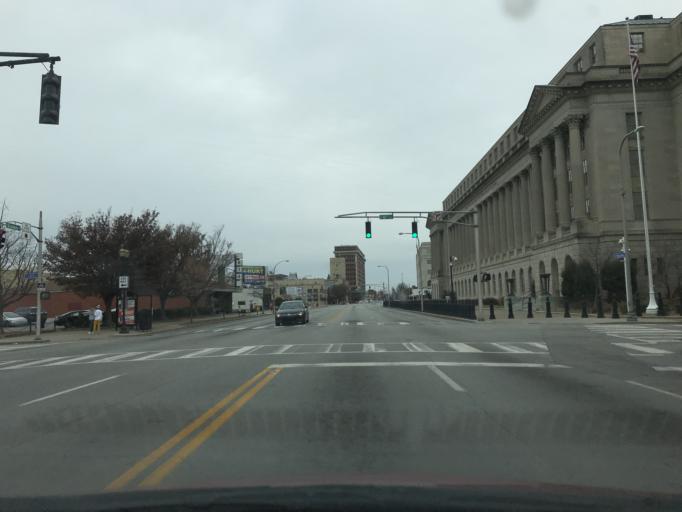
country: US
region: Kentucky
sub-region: Jefferson County
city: Louisville
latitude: 38.2464
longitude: -85.7615
